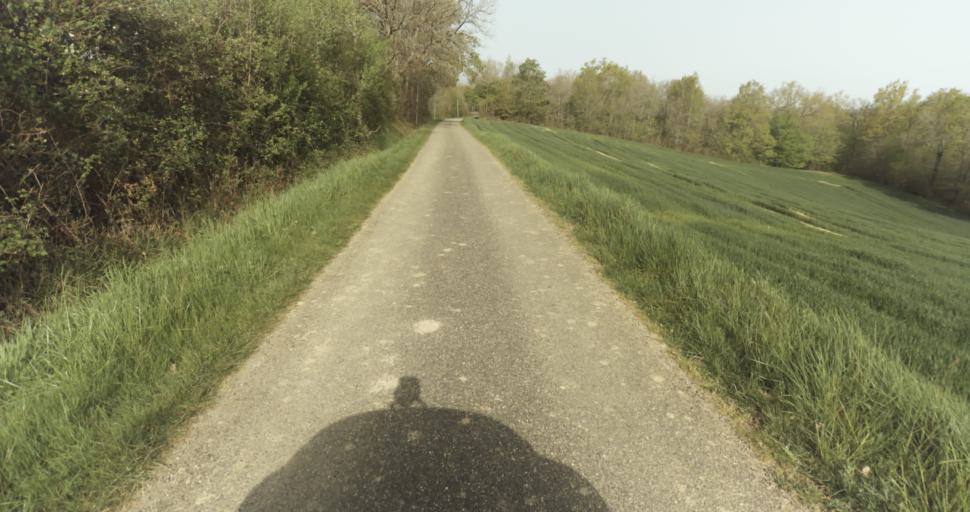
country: FR
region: Midi-Pyrenees
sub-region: Departement du Tarn-et-Garonne
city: Moissac
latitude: 44.1599
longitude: 1.0593
